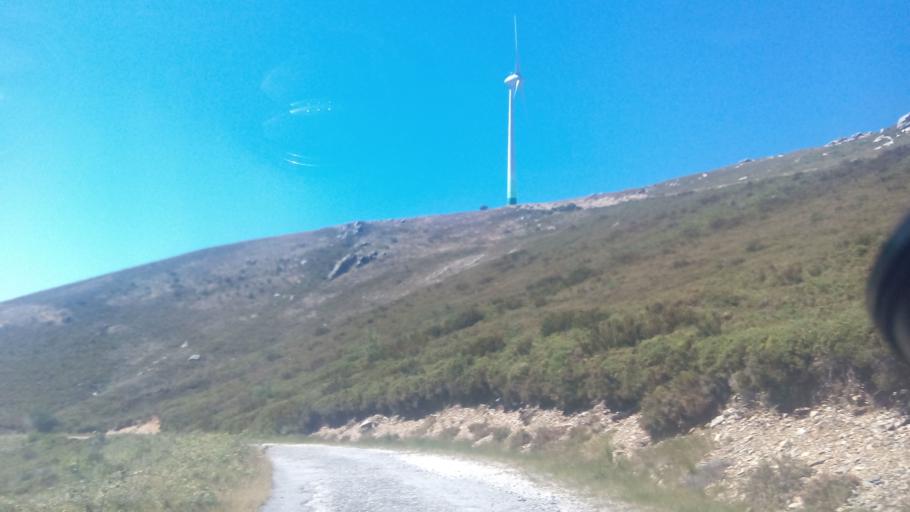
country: PT
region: Vila Real
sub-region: Mesao Frio
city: Mesao Frio
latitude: 41.2652
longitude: -7.8980
